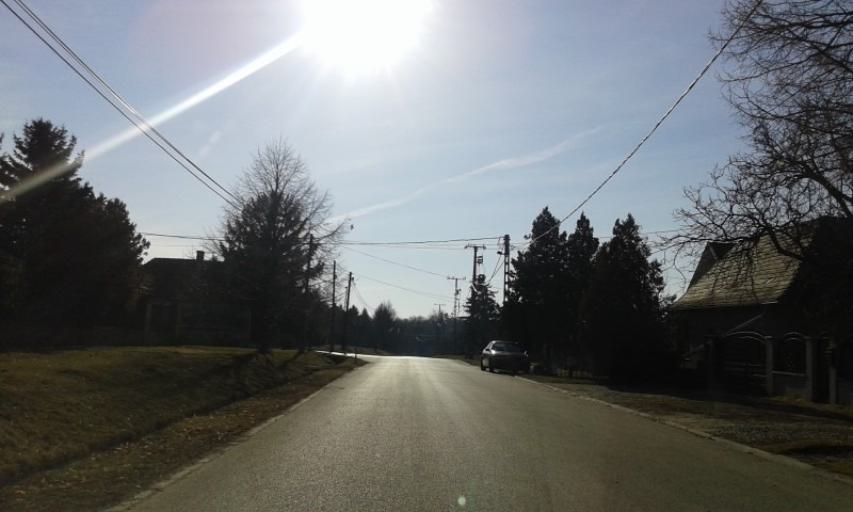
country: HU
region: Pest
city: Soskut
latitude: 47.4053
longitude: 18.7766
